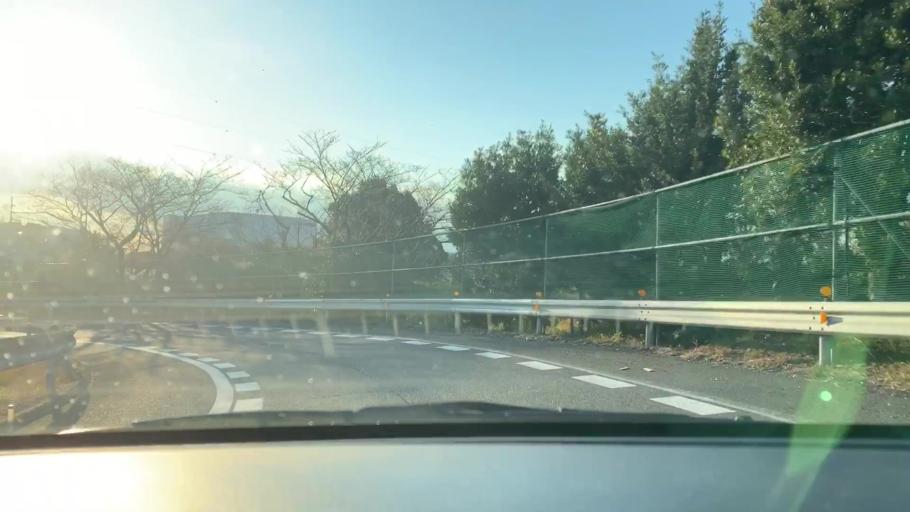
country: JP
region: Chiba
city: Kashiwa
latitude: 35.9093
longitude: 139.9398
